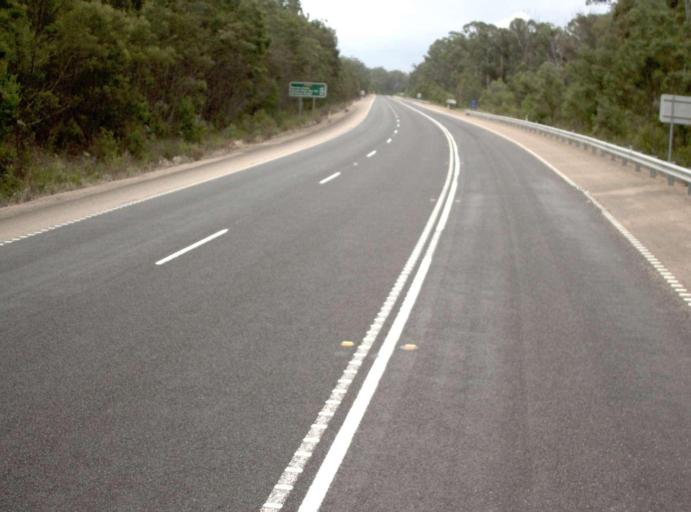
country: AU
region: Victoria
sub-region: East Gippsland
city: Lakes Entrance
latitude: -37.7235
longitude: 148.0859
